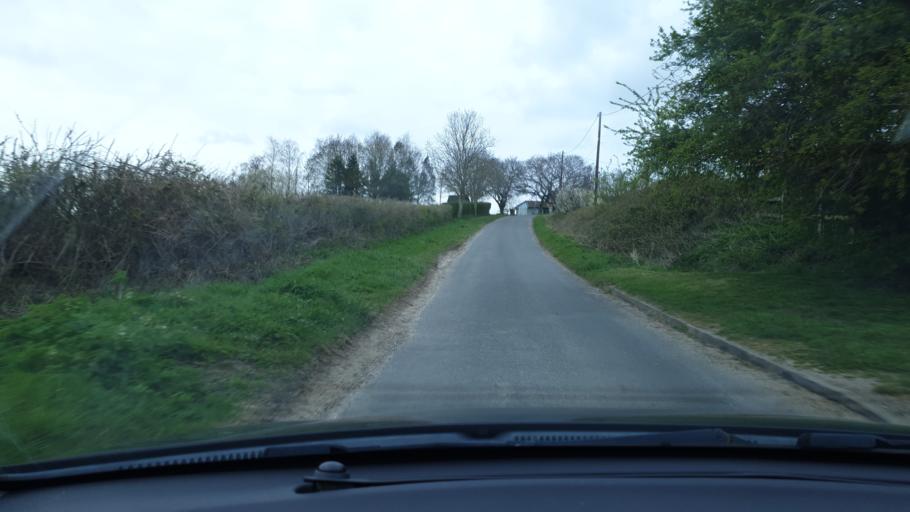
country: GB
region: England
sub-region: Essex
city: Mistley
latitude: 51.9420
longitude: 1.1572
